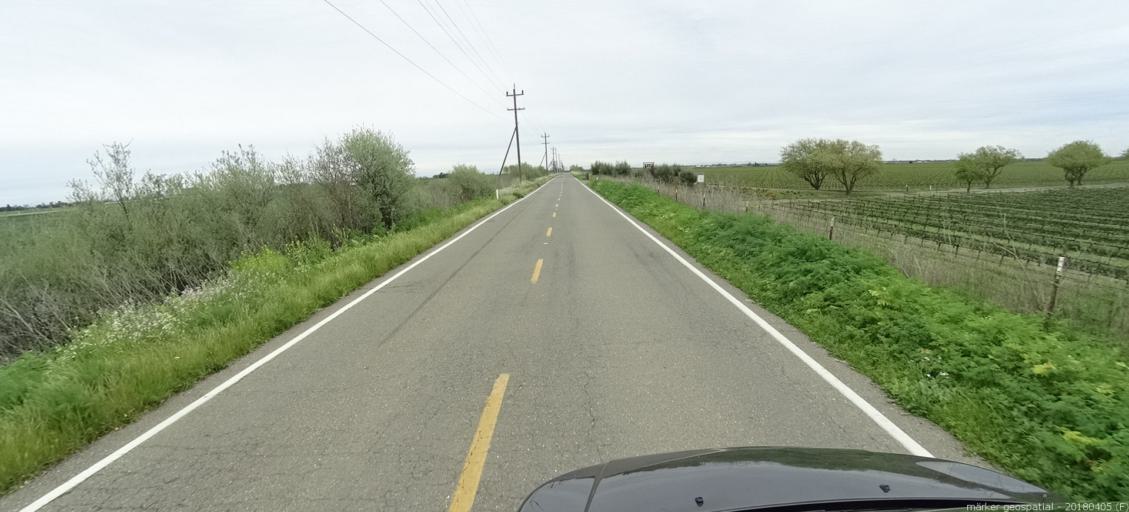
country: US
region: California
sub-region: Sacramento County
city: Walnut Grove
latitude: 38.3205
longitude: -121.4876
